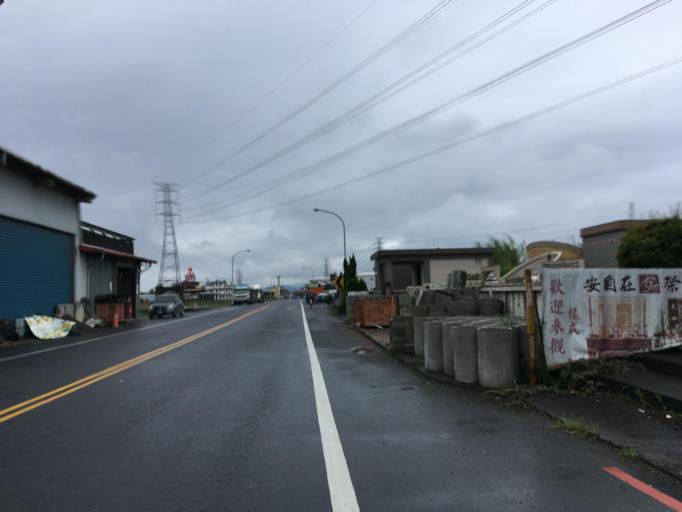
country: TW
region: Taiwan
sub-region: Yilan
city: Yilan
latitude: 24.6637
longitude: 121.7508
